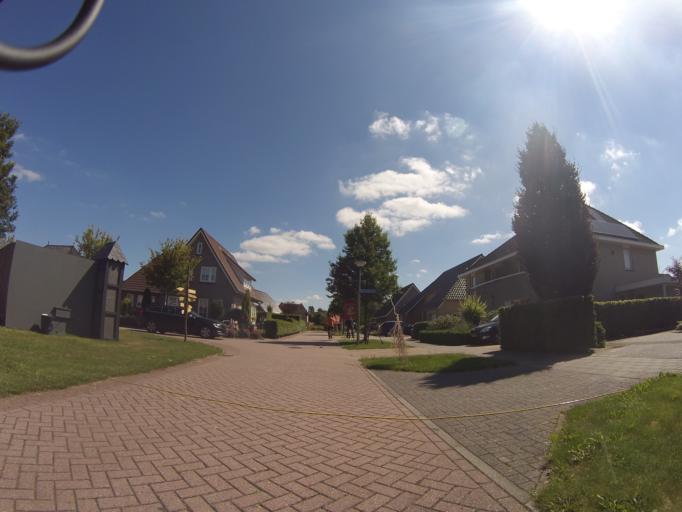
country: NL
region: Drenthe
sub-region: Gemeente Coevorden
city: Sleen
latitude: 52.7639
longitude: 6.8010
